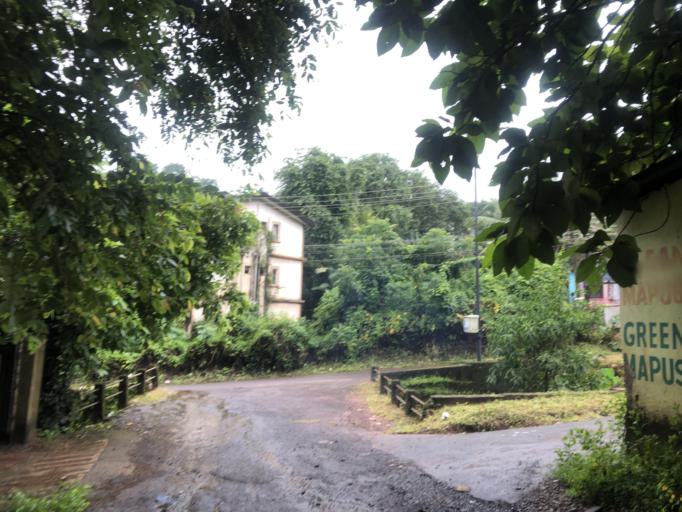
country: IN
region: Goa
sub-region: North Goa
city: Mapuca
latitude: 15.5963
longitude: 73.8041
